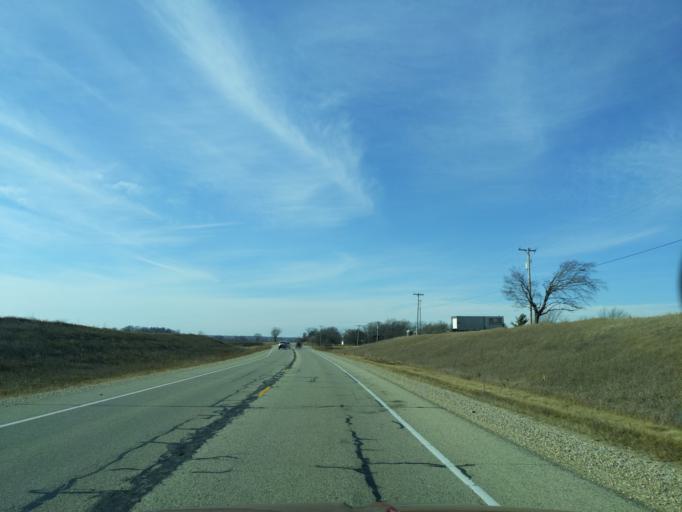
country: US
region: Wisconsin
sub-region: Walworth County
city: Whitewater
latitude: 42.8072
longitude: -88.6670
